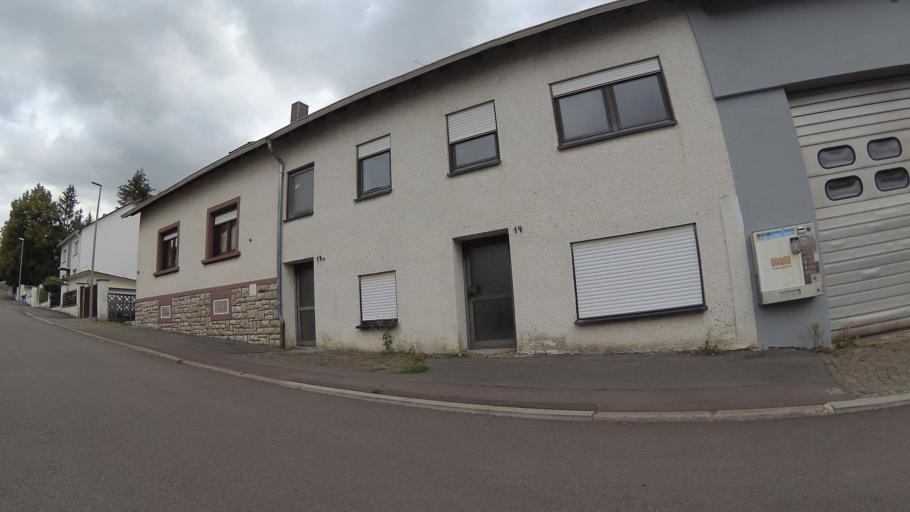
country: DE
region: Saarland
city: Kleinblittersdorf
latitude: 49.1666
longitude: 7.0860
